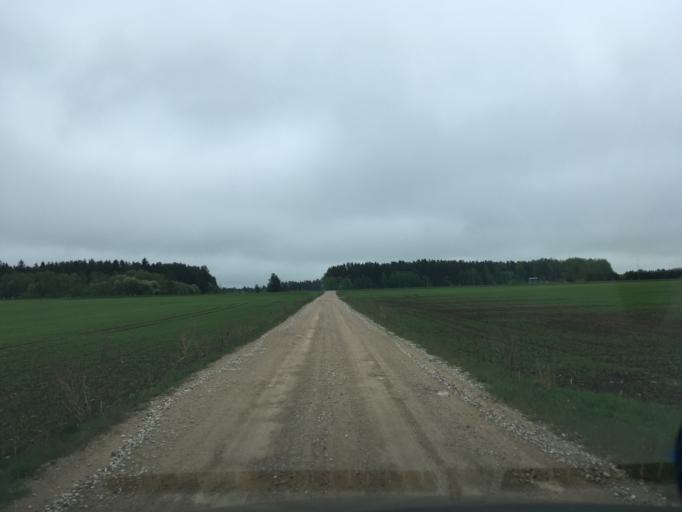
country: EE
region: Harju
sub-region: Rae vald
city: Vaida
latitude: 59.1865
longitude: 25.1106
